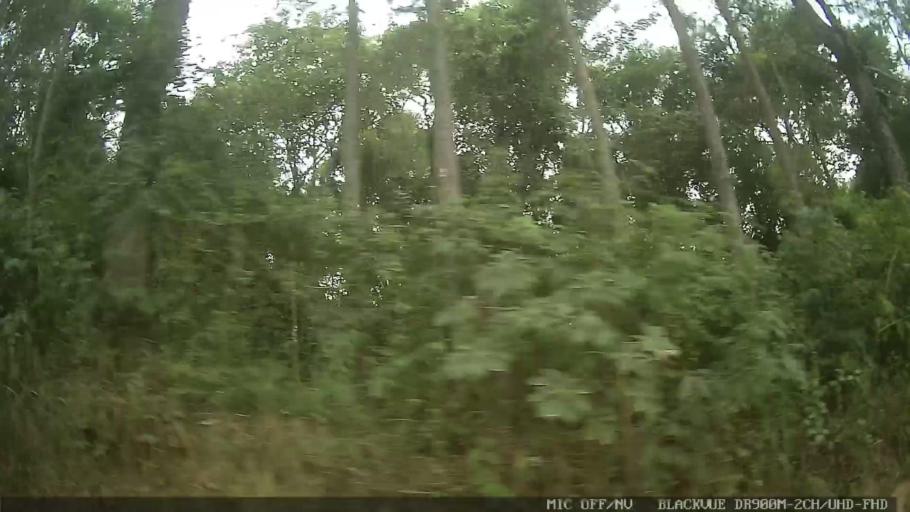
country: BR
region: Sao Paulo
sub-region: Atibaia
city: Atibaia
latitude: -23.1840
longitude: -46.6012
